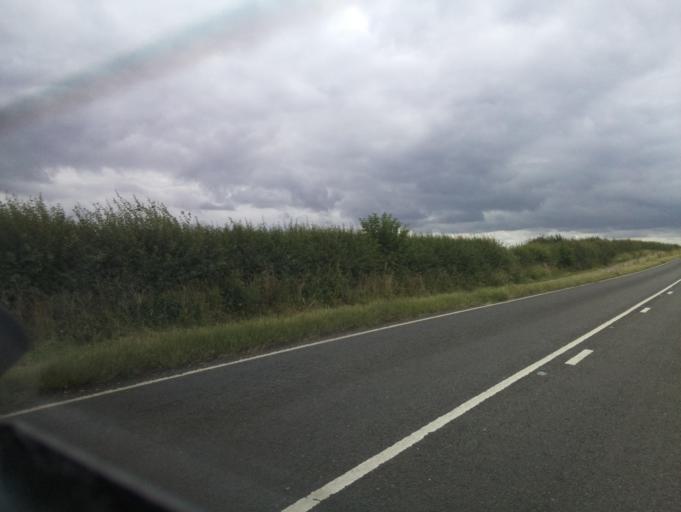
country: GB
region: England
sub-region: District of Rutland
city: Ryhall
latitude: 52.6737
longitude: -0.4699
